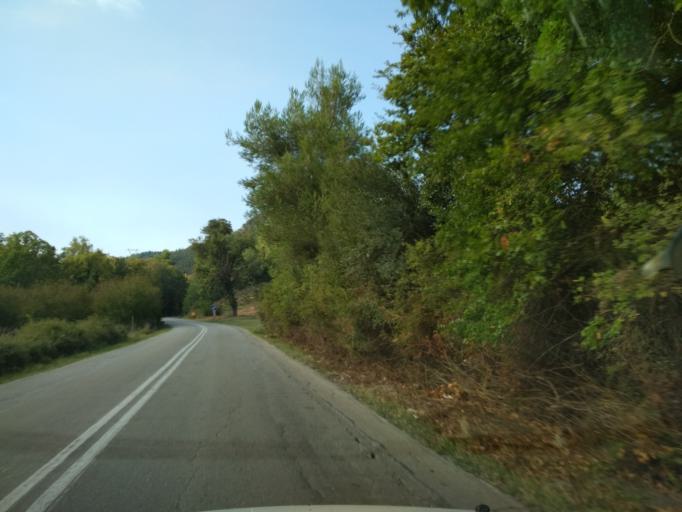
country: GR
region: Central Greece
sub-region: Nomos Evvoias
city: Mantoudi
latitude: 38.7804
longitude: 23.4702
